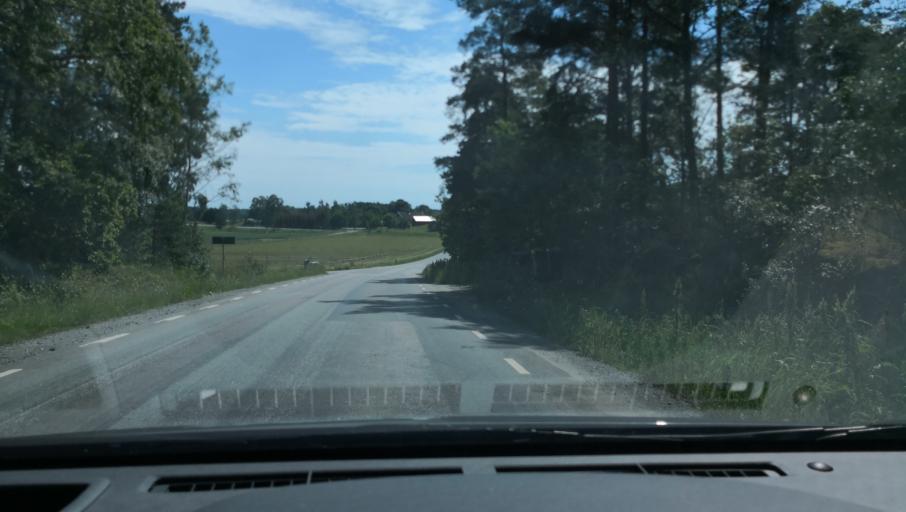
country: SE
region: Uppsala
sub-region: Habo Kommun
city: Balsta
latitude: 59.6404
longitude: 17.4637
